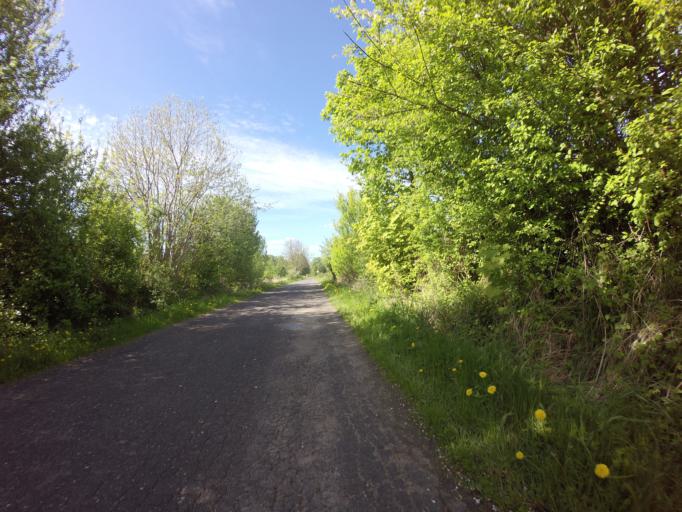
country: PL
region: West Pomeranian Voivodeship
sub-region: Powiat choszczenski
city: Drawno
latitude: 53.2074
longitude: 15.7632
